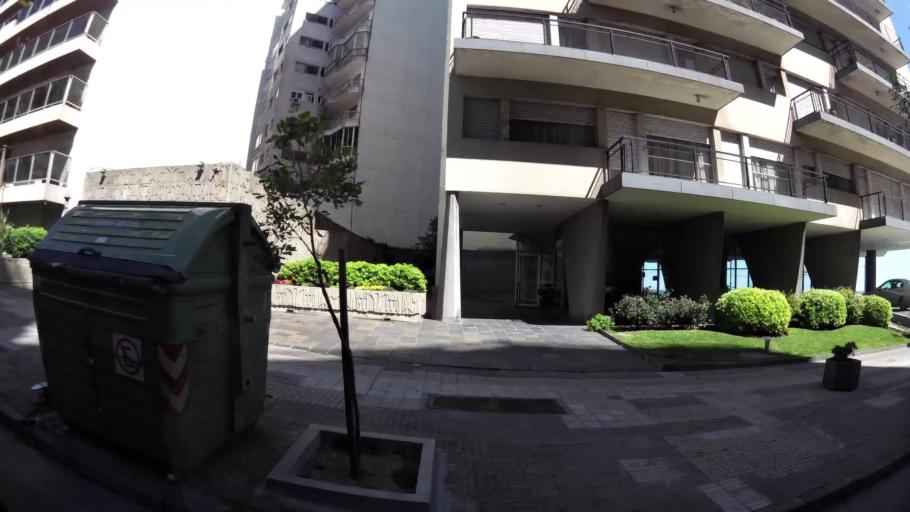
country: UY
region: Montevideo
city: Montevideo
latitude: -34.9089
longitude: -56.1426
